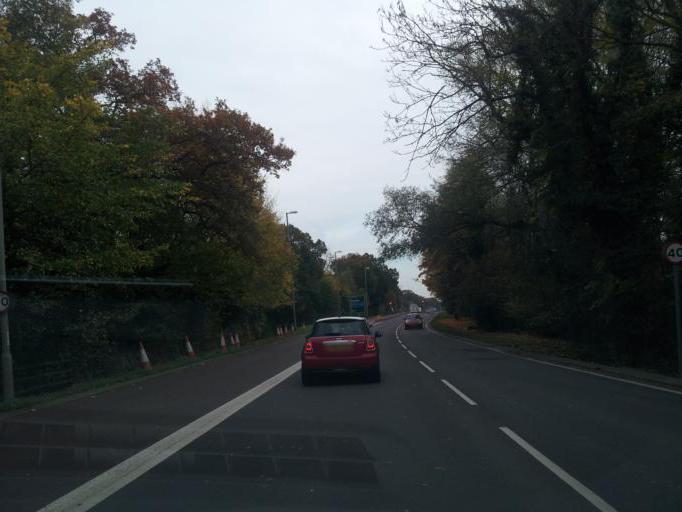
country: GB
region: England
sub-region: Cambridgeshire
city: Girton
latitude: 52.2150
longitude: 0.0733
